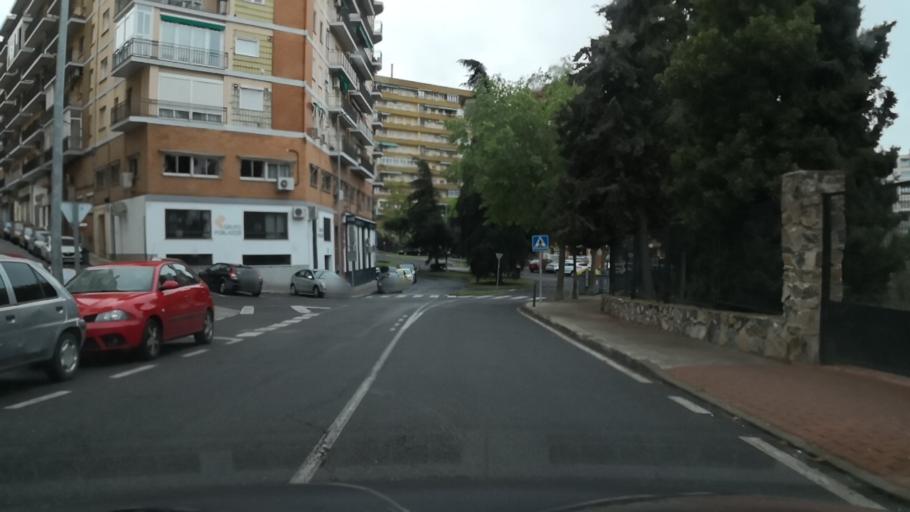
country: ES
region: Extremadura
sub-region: Provincia de Caceres
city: Caceres
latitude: 39.4731
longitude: -6.3821
